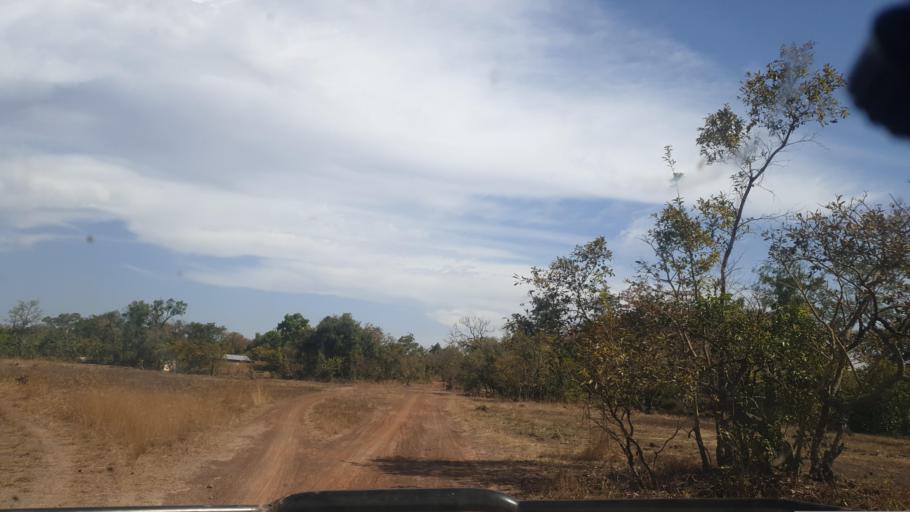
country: ML
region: Sikasso
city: Yanfolila
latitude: 10.4962
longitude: -7.9618
